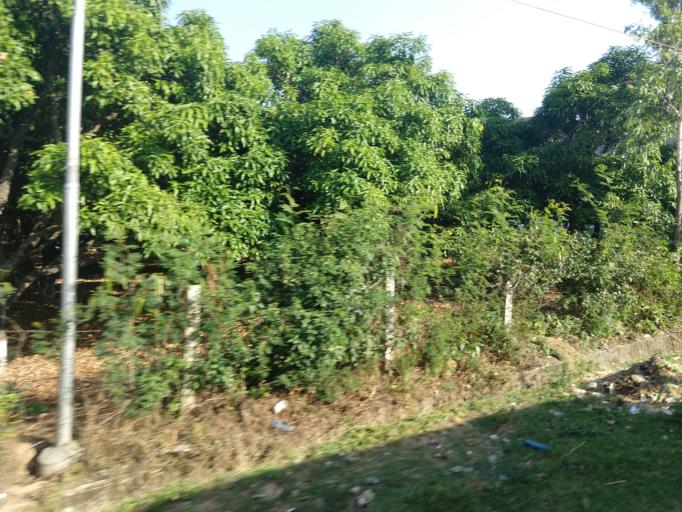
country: IN
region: Himachal Pradesh
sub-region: Chamba
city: Chowari
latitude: 32.3510
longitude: 75.9135
